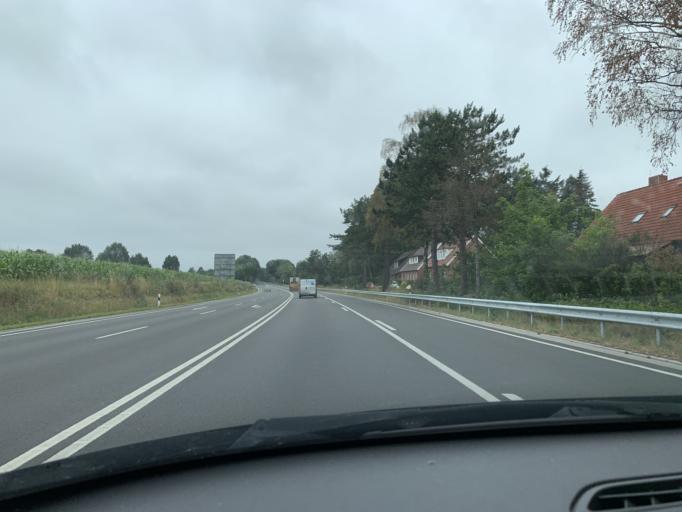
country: DE
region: Lower Saxony
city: Haselunne
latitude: 52.6761
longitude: 7.5008
